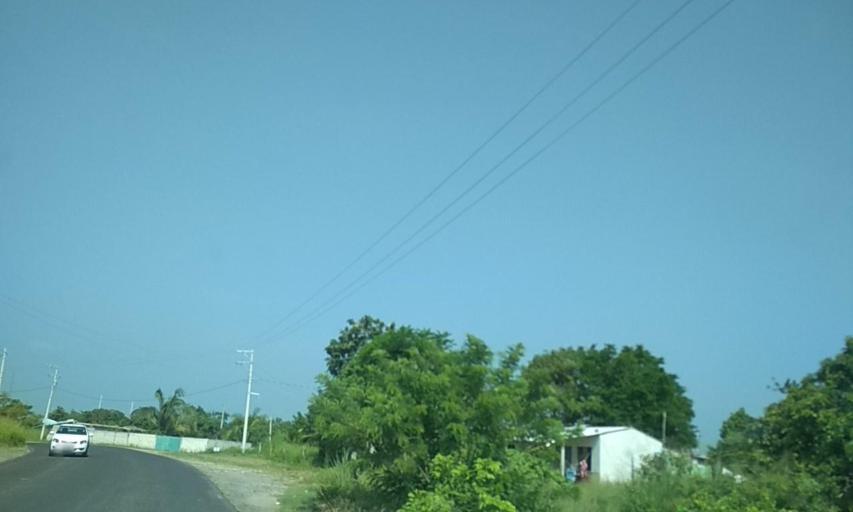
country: MX
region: Veracruz
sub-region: Atzalan
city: Colonias Pedernales
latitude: 20.0529
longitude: -96.9916
